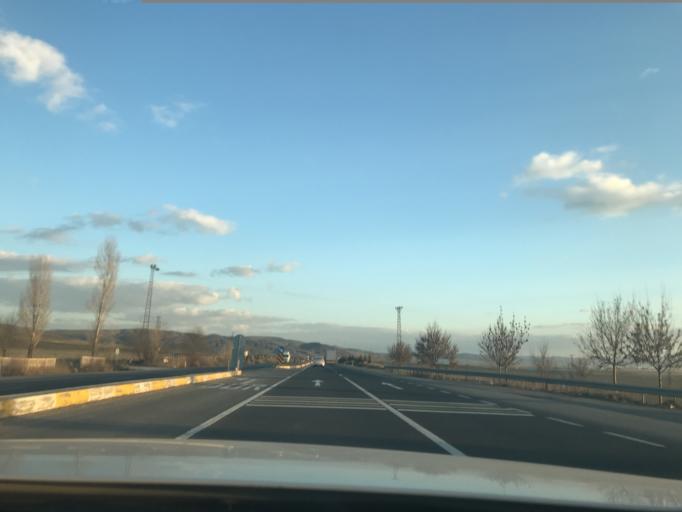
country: TR
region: Ankara
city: Altpinar
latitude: 39.3817
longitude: 32.8928
